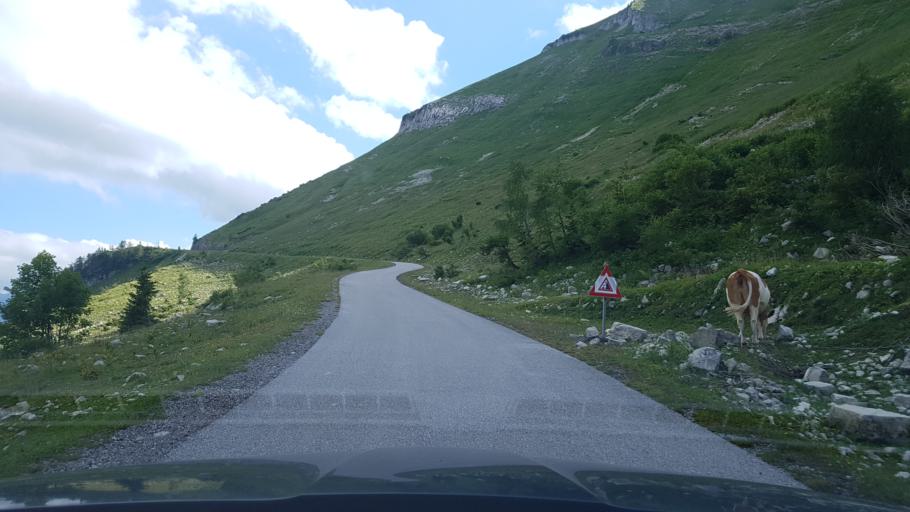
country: AT
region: Salzburg
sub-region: Politischer Bezirk Salzburg-Umgebung
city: Hintersee
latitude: 47.6458
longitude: 13.2795
